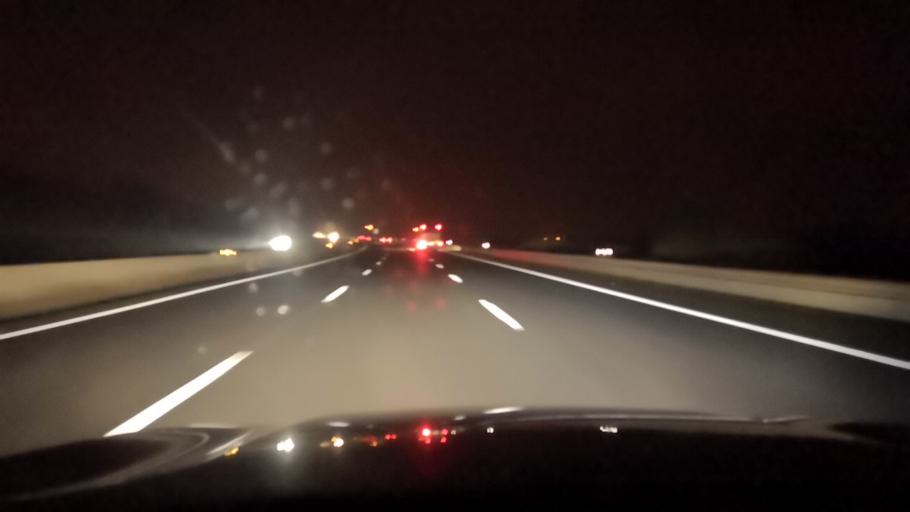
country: PT
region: Santarem
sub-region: Cartaxo
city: Pontevel
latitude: 39.1607
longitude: -8.8629
